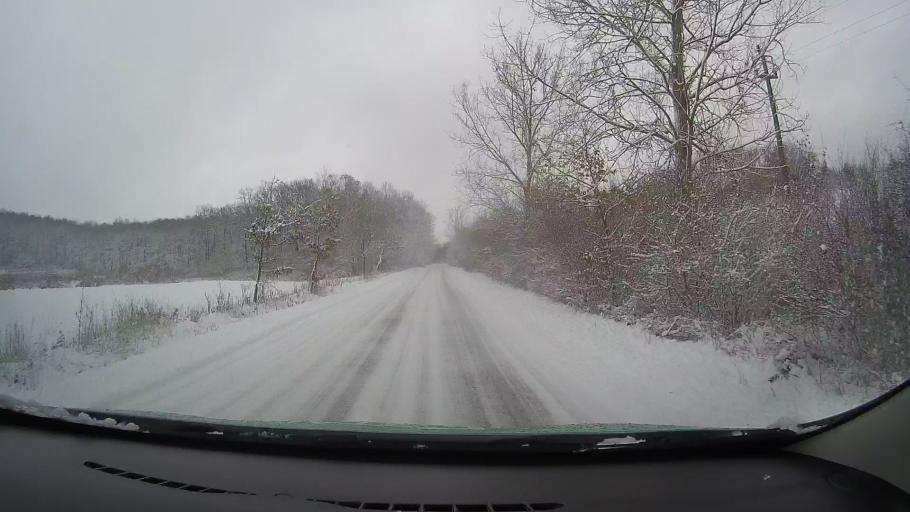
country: RO
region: Hunedoara
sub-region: Comuna Pestisu Mic
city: Pestisu Mic
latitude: 45.8143
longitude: 22.8974
